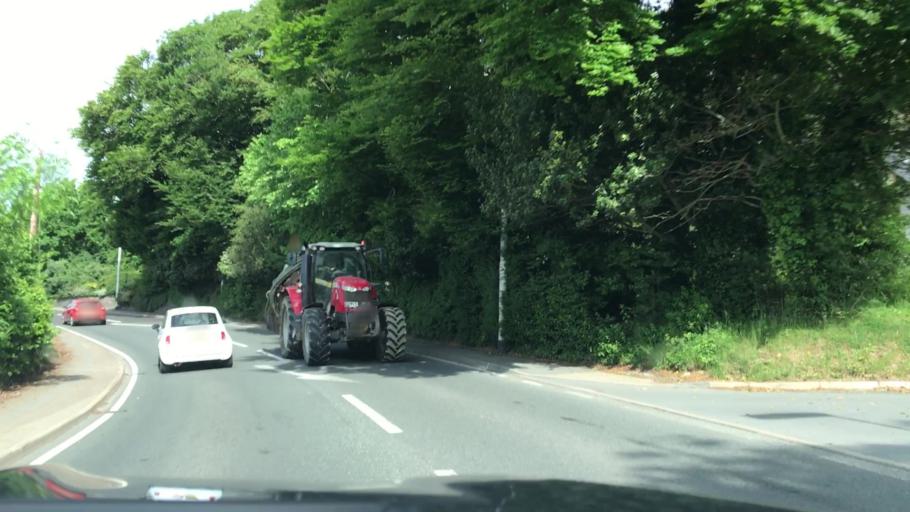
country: GB
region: Wales
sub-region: County of Ceredigion
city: Penparcau
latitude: 52.4059
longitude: -4.0536
